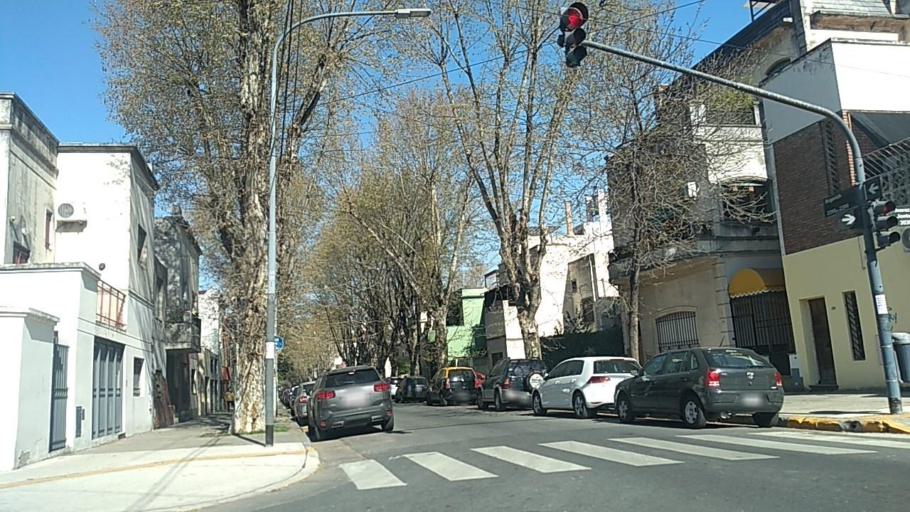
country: AR
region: Buenos Aires F.D.
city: Villa Santa Rita
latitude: -34.6092
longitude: -58.4849
